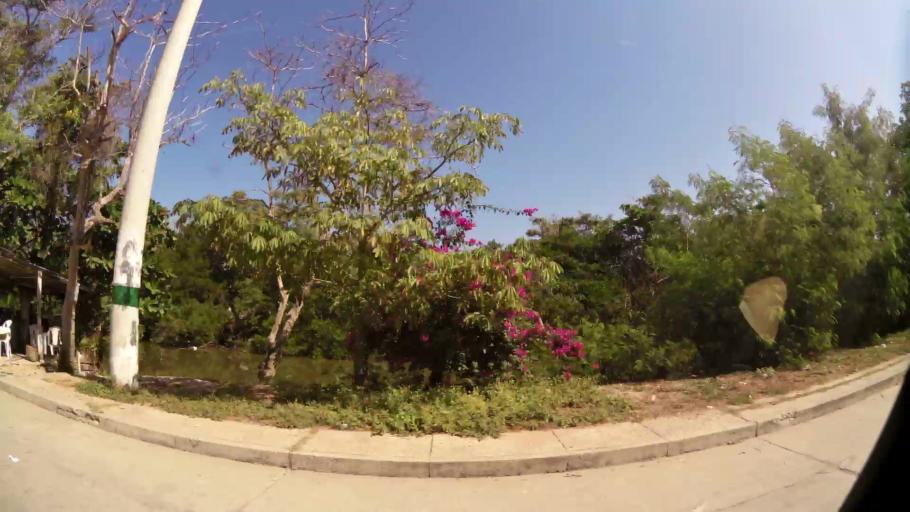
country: CO
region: Bolivar
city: Cartagena
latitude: 10.4406
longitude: -75.5142
